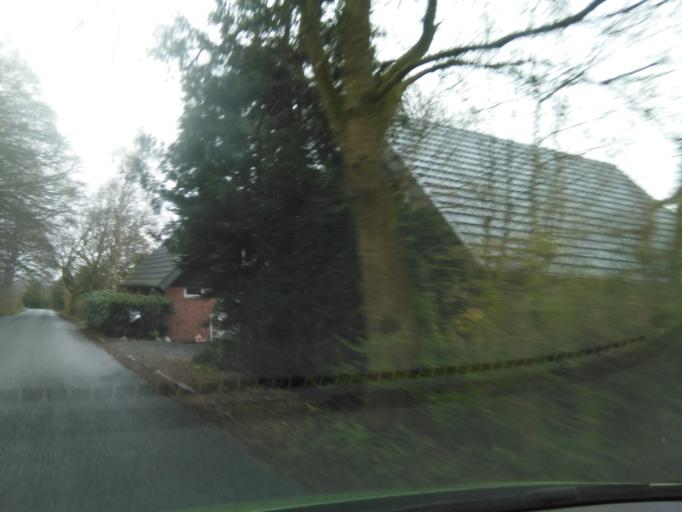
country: DK
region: Central Jutland
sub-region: Arhus Kommune
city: Kolt
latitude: 56.1505
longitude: 10.0802
